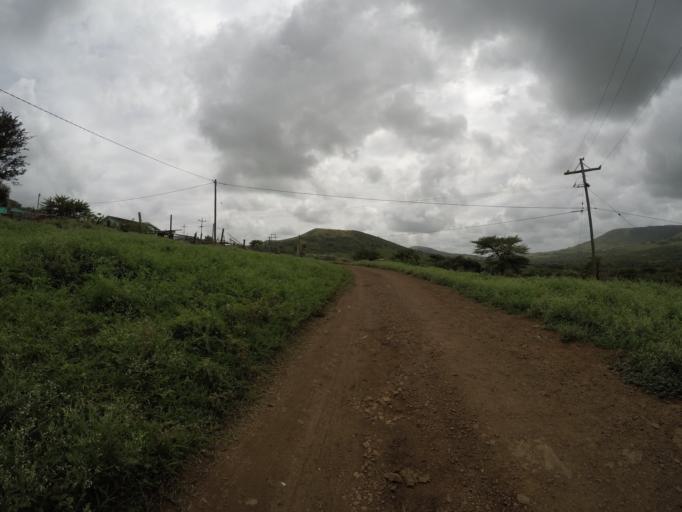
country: ZA
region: KwaZulu-Natal
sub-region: uThungulu District Municipality
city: Empangeni
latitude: -28.5896
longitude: 31.8885
